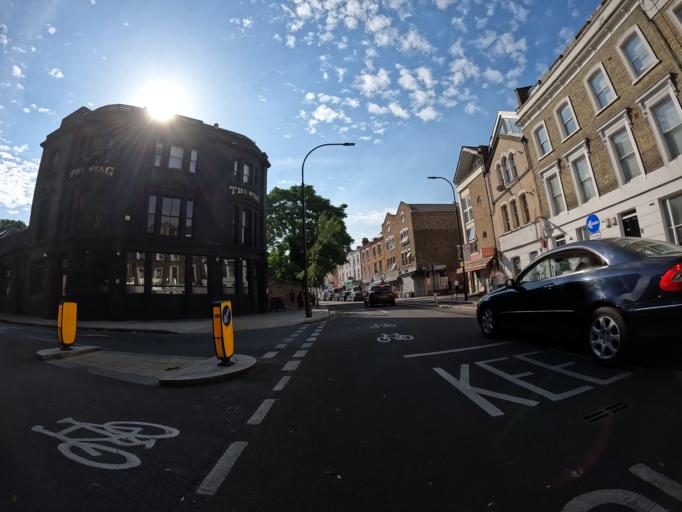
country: GB
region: England
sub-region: Greater London
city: Hendon
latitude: 51.5795
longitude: -0.2024
